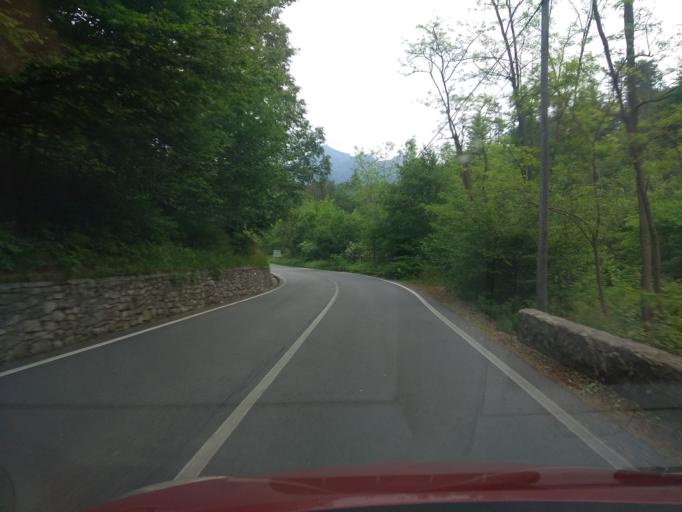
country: IT
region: Piedmont
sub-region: Provincia di Biella
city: Pray
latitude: 45.6598
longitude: 8.2006
